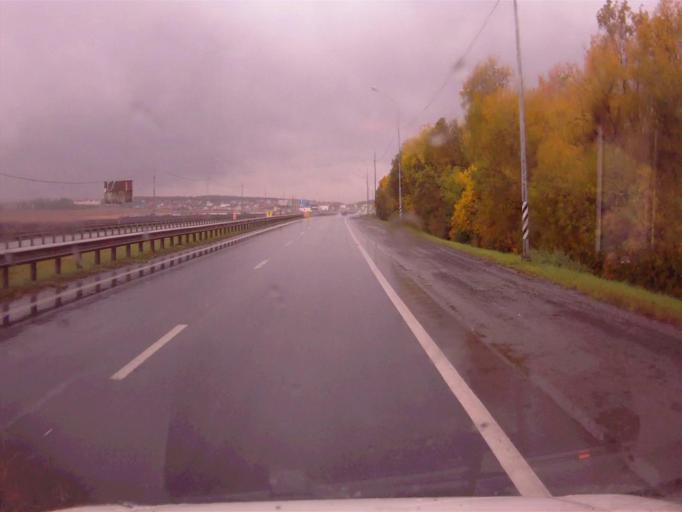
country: RU
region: Chelyabinsk
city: Dolgoderevenskoye
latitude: 55.2691
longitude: 61.3448
